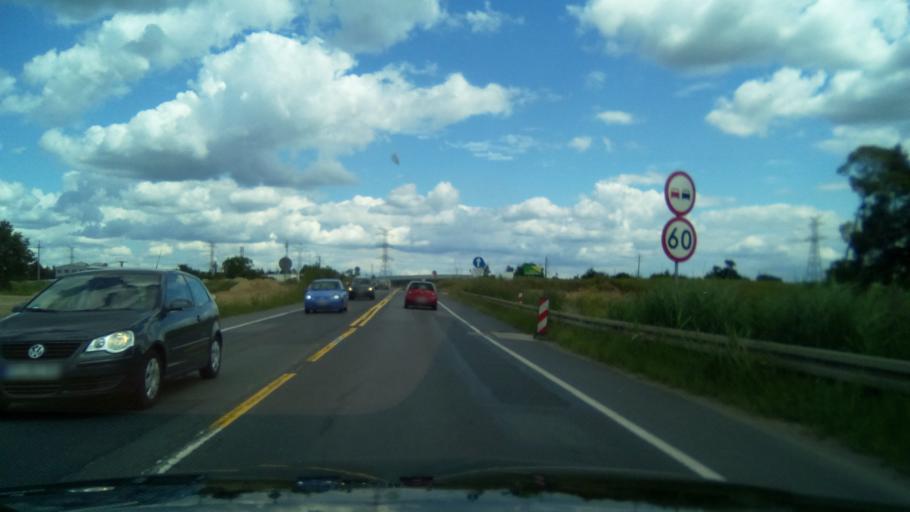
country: PL
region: Kujawsko-Pomorskie
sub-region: Powiat bydgoski
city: Biale Blota
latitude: 53.0822
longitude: 17.8663
